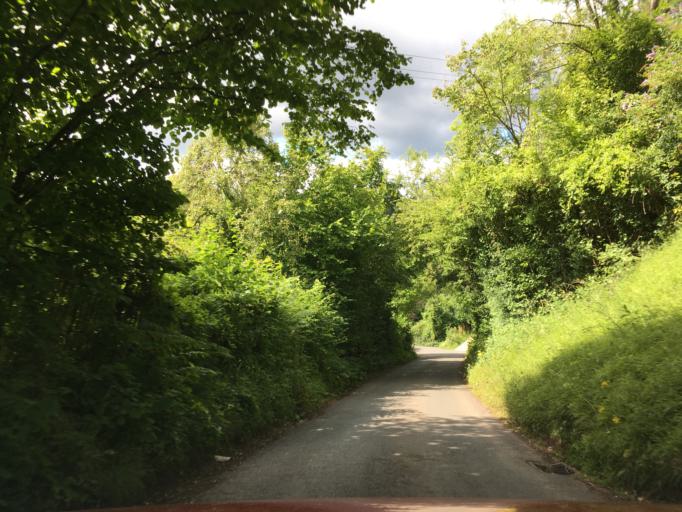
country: GB
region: England
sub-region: Gloucestershire
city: Cinderford
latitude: 51.8259
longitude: -2.4548
